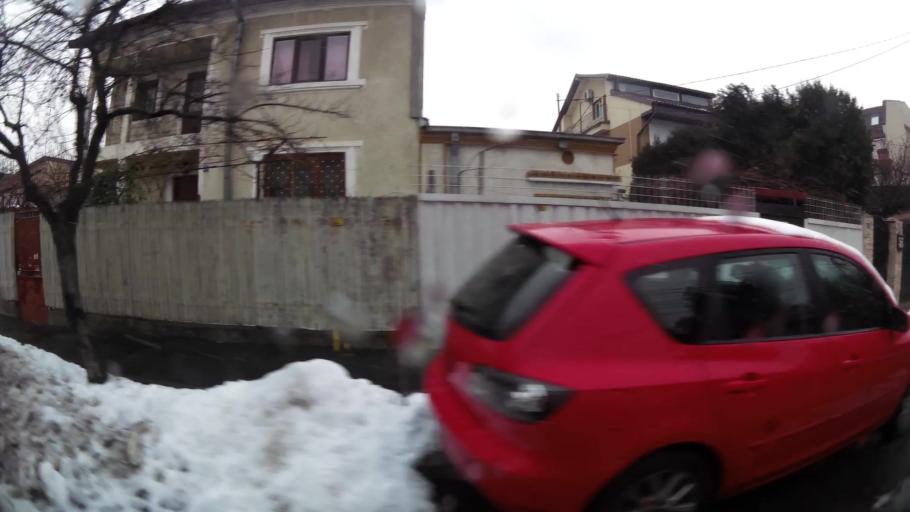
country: RO
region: Ilfov
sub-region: Comuna Chiajna
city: Rosu
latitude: 44.4937
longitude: 26.0362
